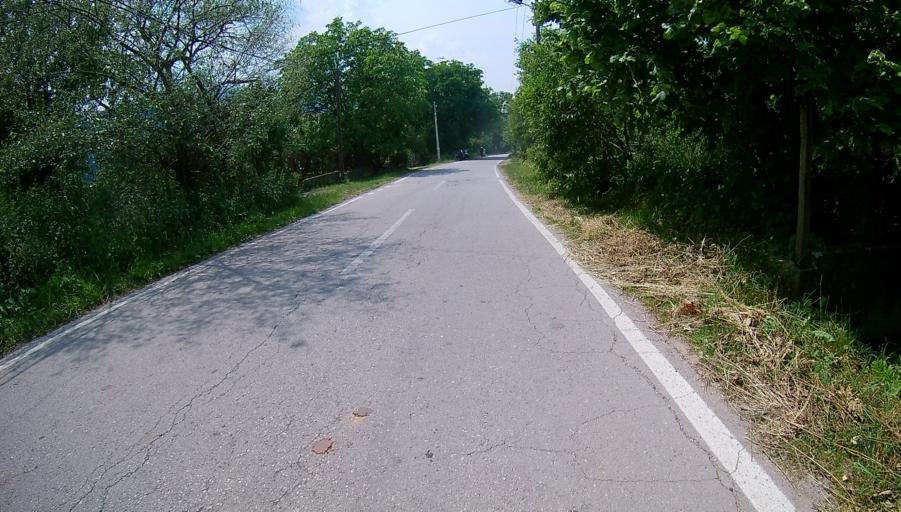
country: RS
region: Central Serbia
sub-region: Nisavski Okrug
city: Gadzin Han
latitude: 43.1633
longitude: 22.1048
